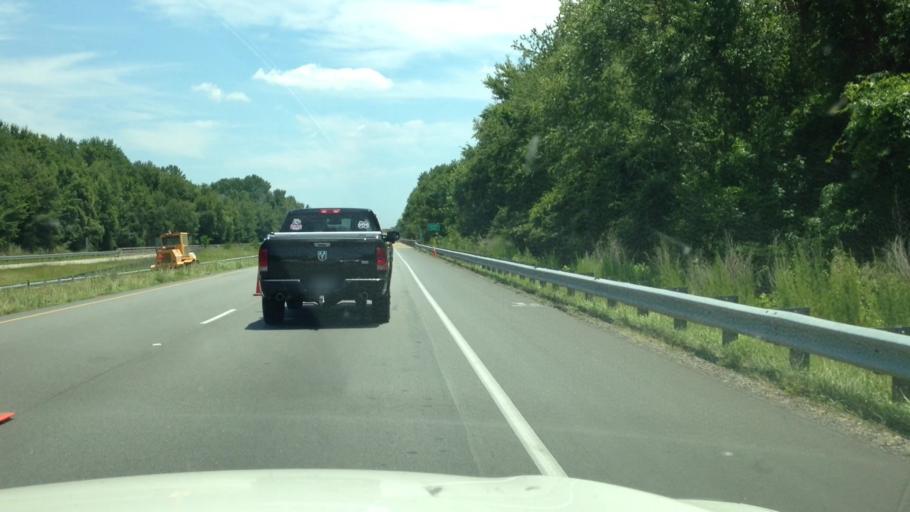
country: US
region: South Carolina
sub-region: Lee County
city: Bishopville
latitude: 34.1873
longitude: -80.1959
